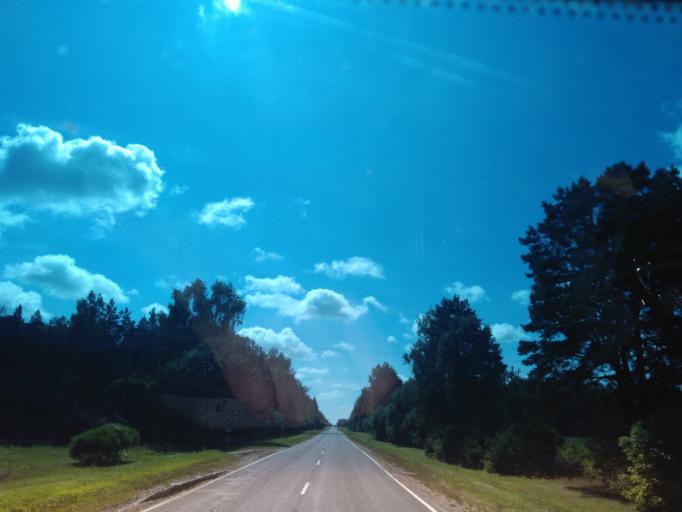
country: BY
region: Minsk
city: Uzda
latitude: 53.3436
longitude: 27.2279
